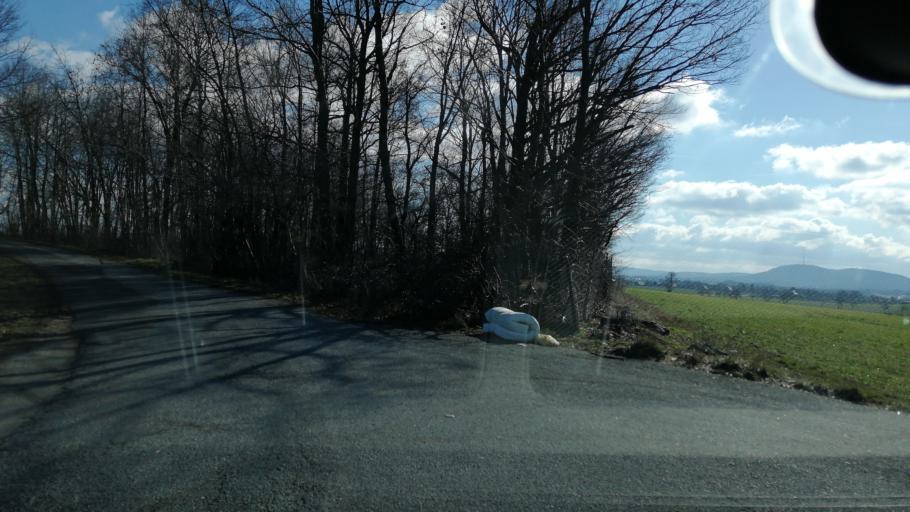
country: DE
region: Saxony
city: Weissenberg
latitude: 51.1604
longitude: 14.7206
